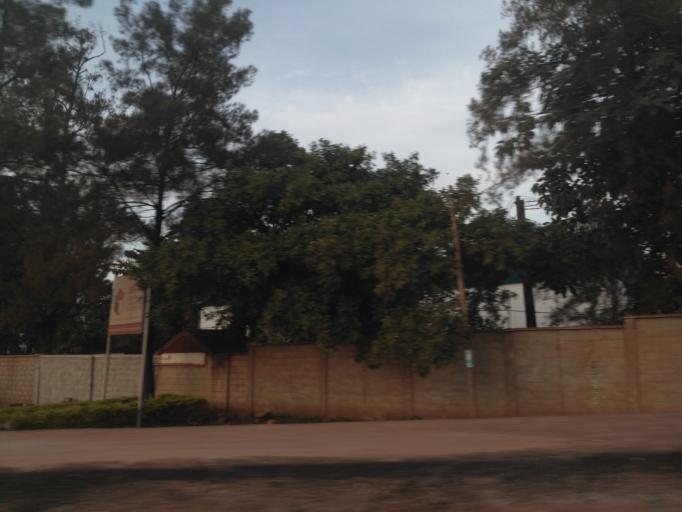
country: UG
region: Central Region
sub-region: Buikwe District
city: Njeru
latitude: 0.4398
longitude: 33.1804
